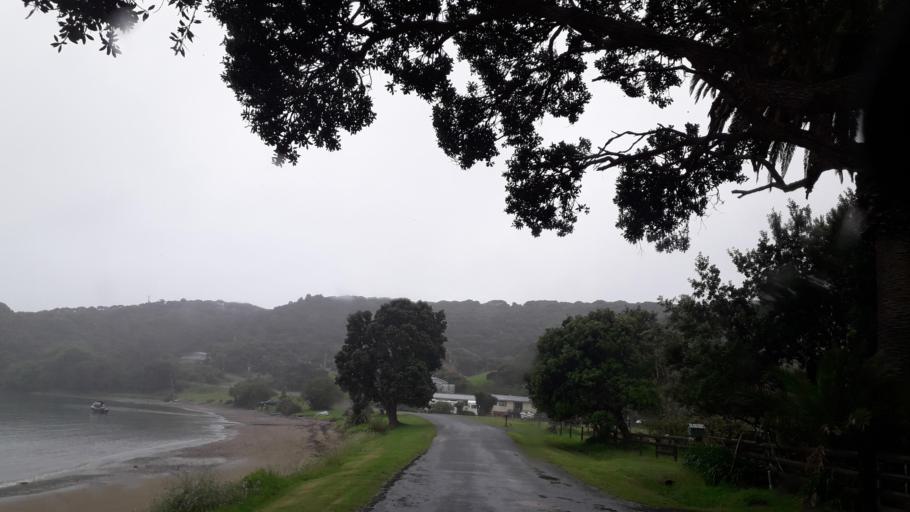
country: NZ
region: Northland
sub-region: Far North District
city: Paihia
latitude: -35.2263
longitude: 174.2636
